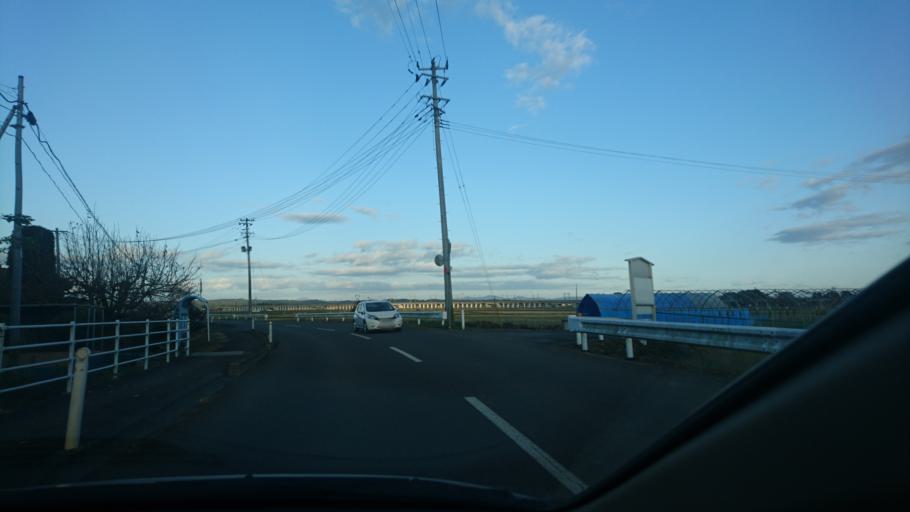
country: JP
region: Iwate
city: Ichinoseki
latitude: 38.7765
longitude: 141.0800
